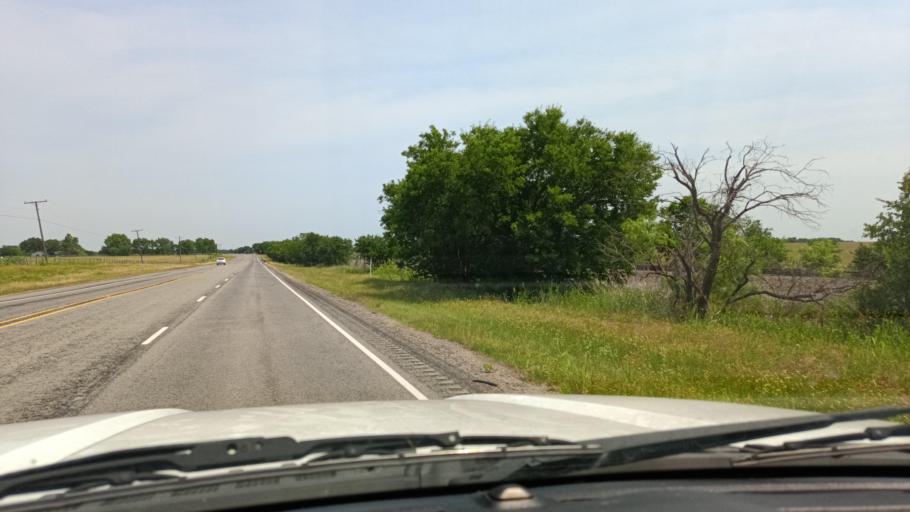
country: US
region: Texas
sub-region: Bell County
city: Rogers
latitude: 30.8622
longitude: -97.1124
